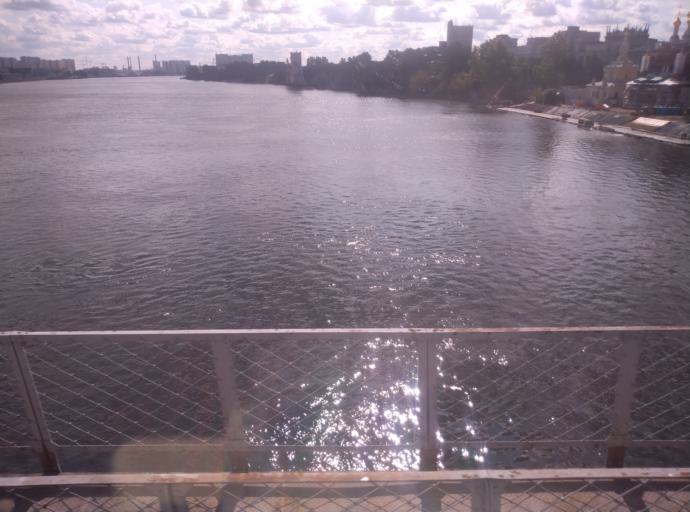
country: RU
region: St.-Petersburg
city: Centralniy
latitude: 59.9146
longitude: 30.4072
